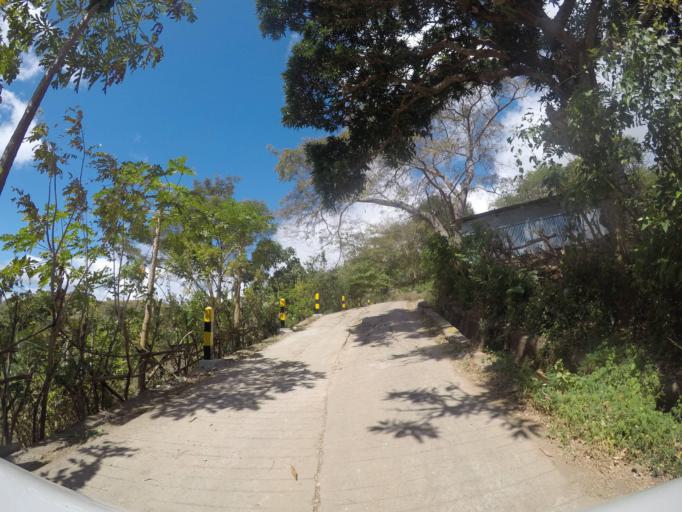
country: TL
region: Lautem
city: Lospalos
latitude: -8.5394
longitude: 126.8031
